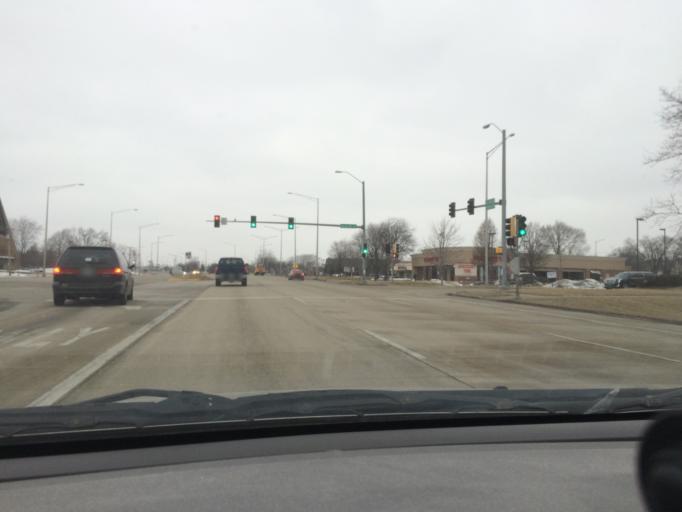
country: US
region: Illinois
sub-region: Cook County
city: Hoffman Estates
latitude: 42.0472
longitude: -88.0888
